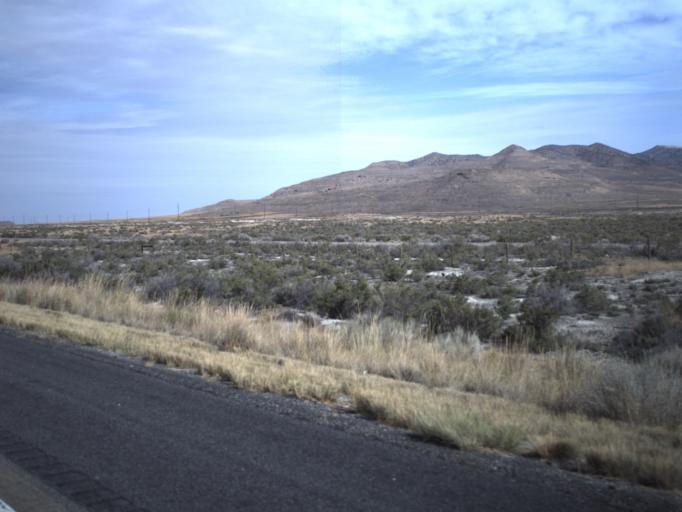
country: US
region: Utah
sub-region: Tooele County
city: Grantsville
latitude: 40.7830
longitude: -112.8180
